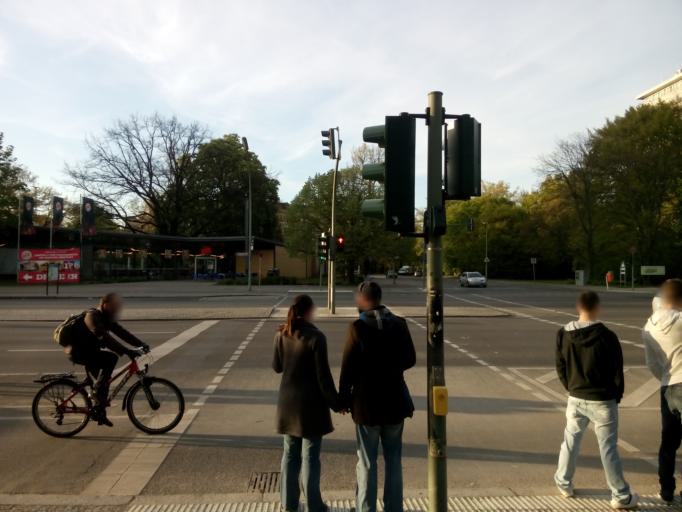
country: DE
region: Berlin
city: Hansaviertel
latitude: 52.5134
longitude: 13.3379
